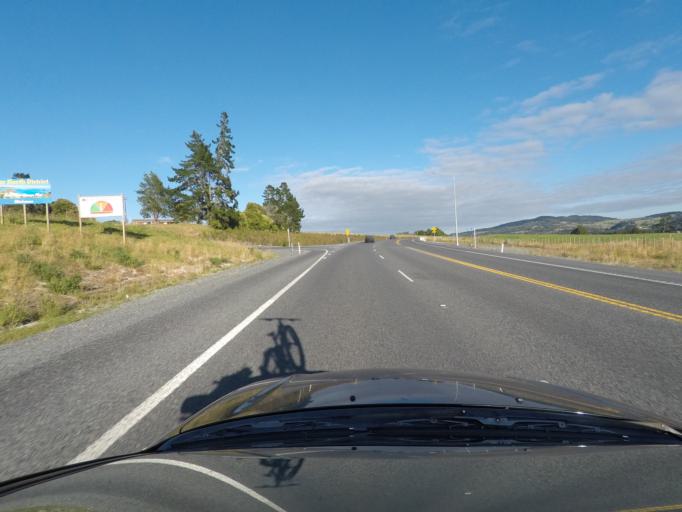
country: NZ
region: Northland
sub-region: Far North District
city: Kawakawa
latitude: -35.5109
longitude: 174.1797
